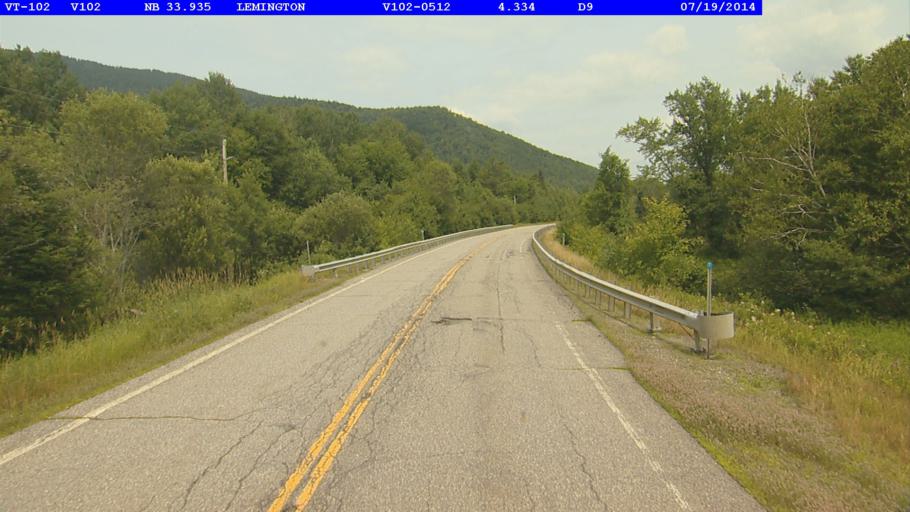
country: US
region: New Hampshire
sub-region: Coos County
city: Colebrook
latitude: 44.8768
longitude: -71.5297
